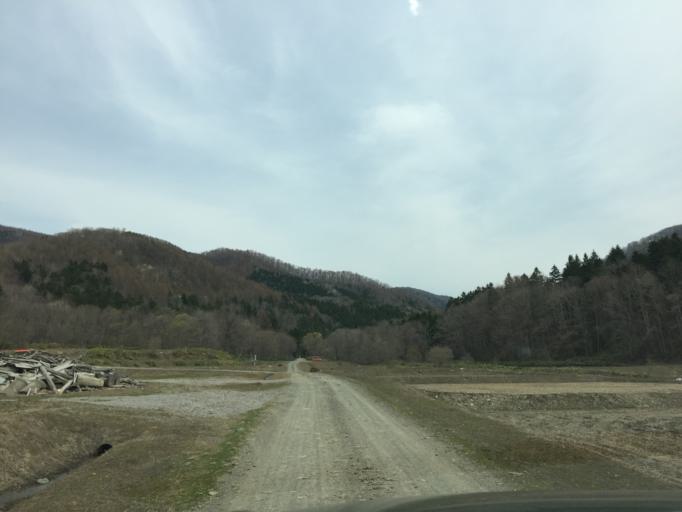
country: JP
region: Hokkaido
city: Ashibetsu
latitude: 43.6229
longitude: 142.2255
